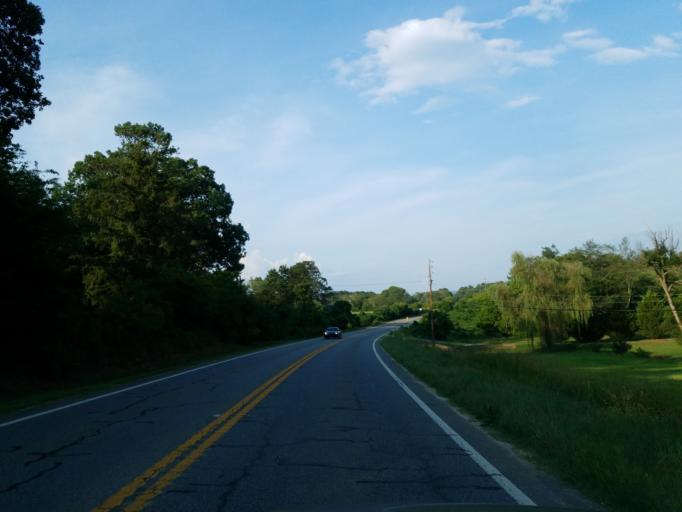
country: US
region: Georgia
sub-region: Pickens County
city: Jasper
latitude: 34.5153
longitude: -84.5425
